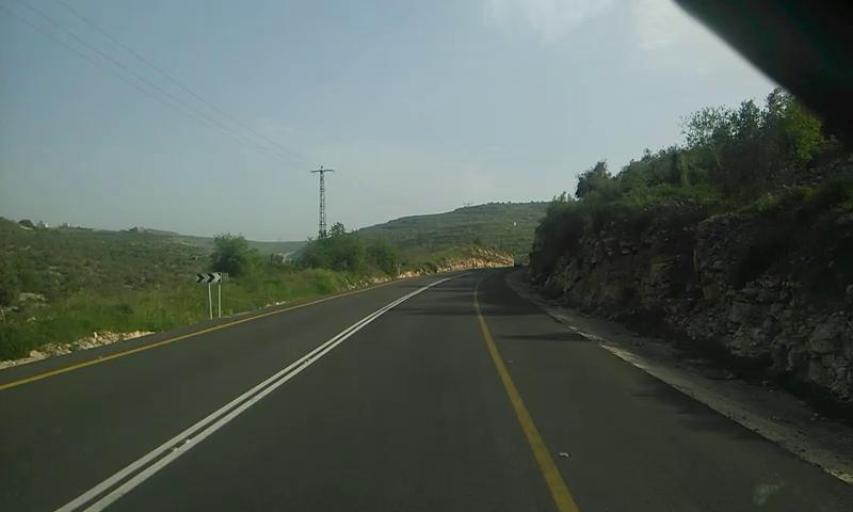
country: PS
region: West Bank
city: Jit
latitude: 32.2191
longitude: 35.1746
